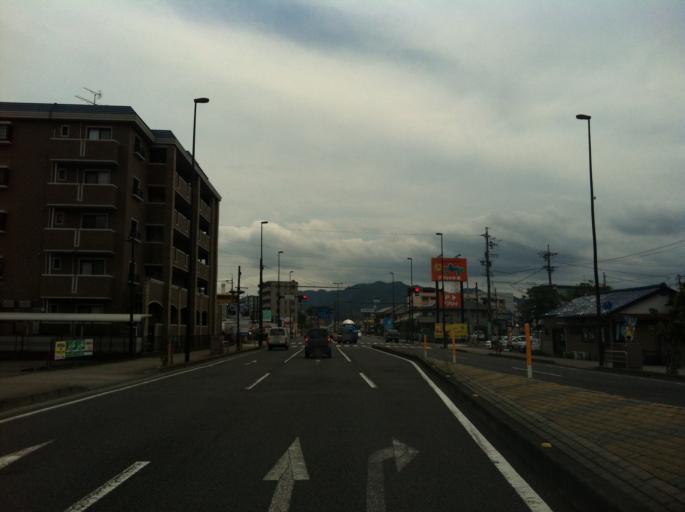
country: JP
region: Shizuoka
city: Shizuoka-shi
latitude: 34.9568
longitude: 138.3856
